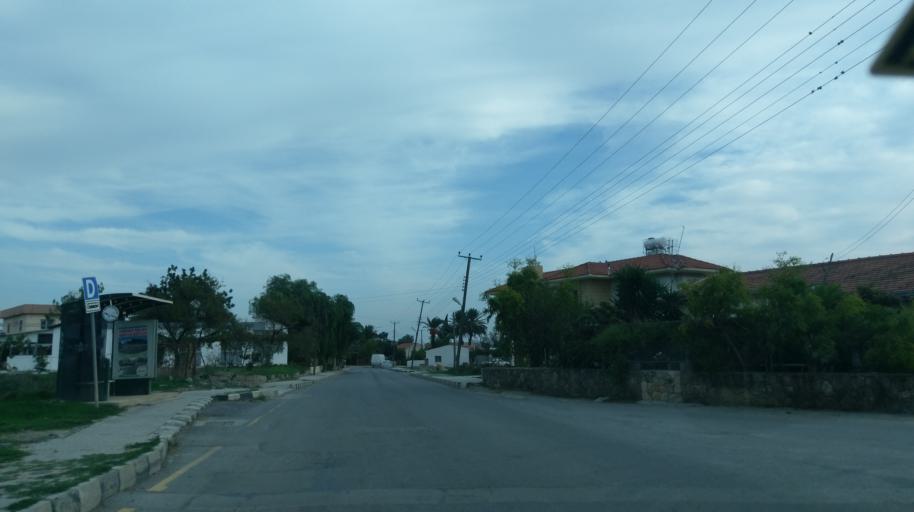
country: CY
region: Keryneia
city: Kyrenia
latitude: 35.2696
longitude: 33.3181
